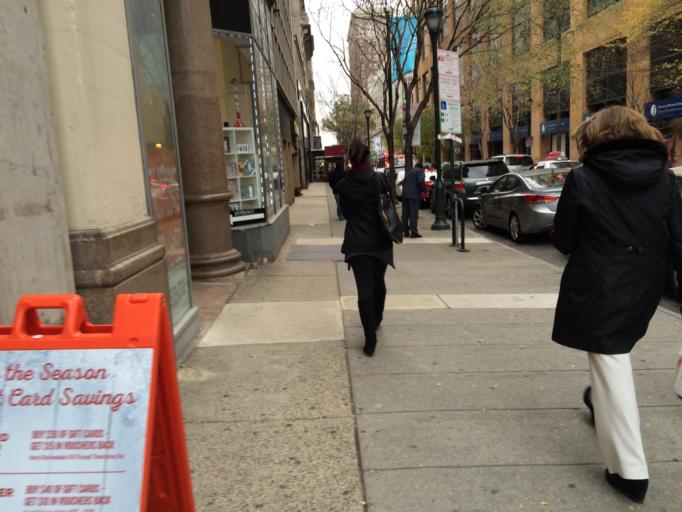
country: US
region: Pennsylvania
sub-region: Philadelphia County
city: Philadelphia
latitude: 39.9502
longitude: -75.1585
